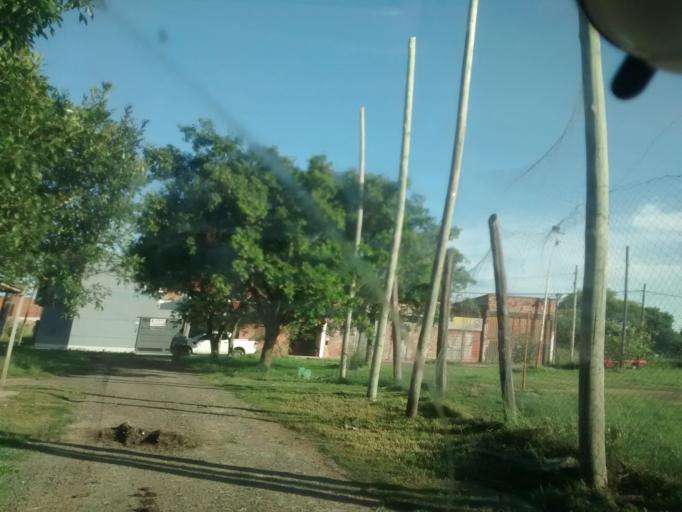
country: AR
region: Chaco
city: Fontana
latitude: -27.4459
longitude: -59.0178
